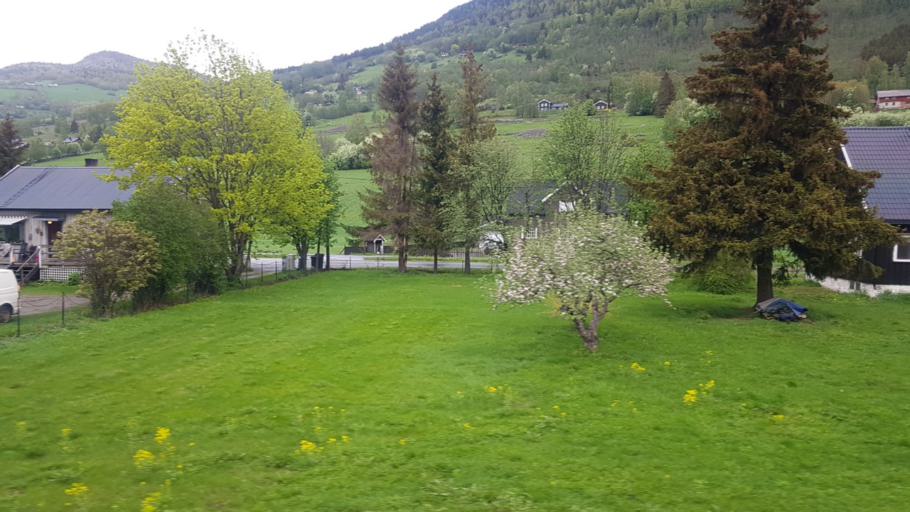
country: NO
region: Oppland
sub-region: Nord-Fron
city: Vinstra
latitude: 61.6639
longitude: 9.6759
